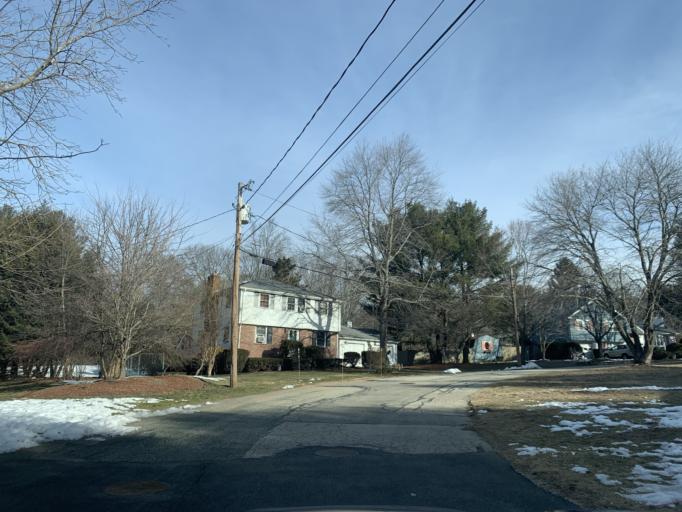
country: US
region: Massachusetts
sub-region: Norfolk County
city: Norwood
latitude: 42.2072
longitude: -71.1707
